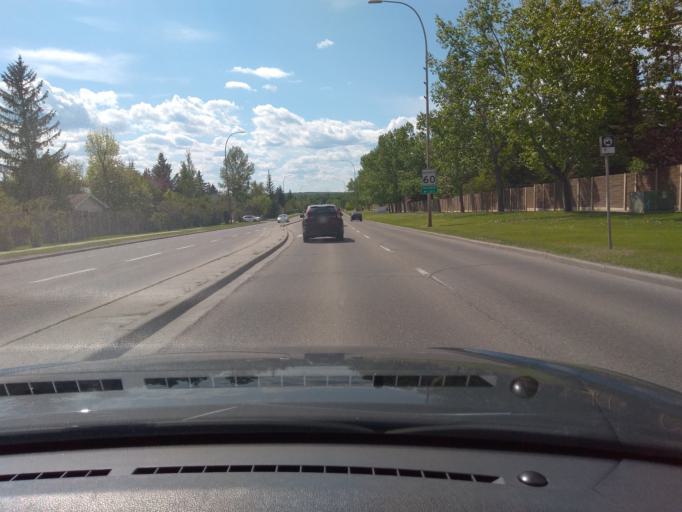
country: CA
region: Alberta
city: Calgary
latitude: 50.9722
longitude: -114.1121
